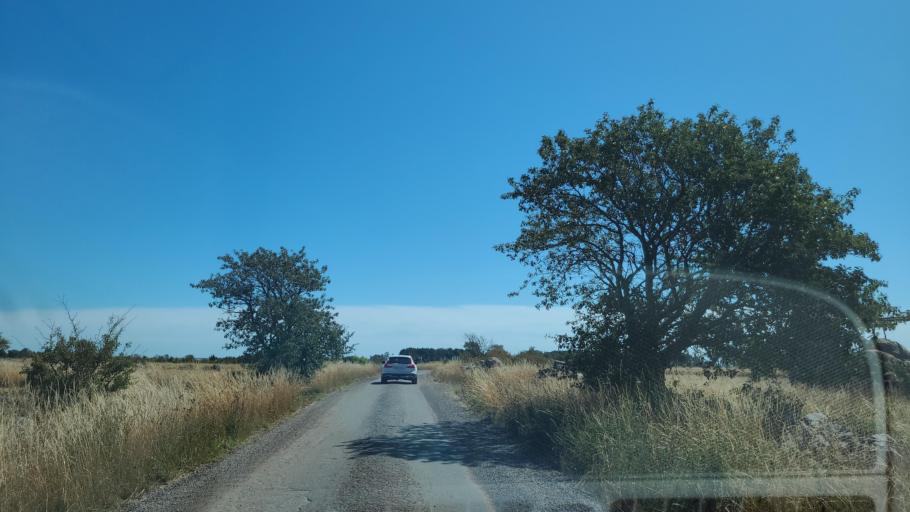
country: SE
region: Kalmar
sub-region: Morbylanga Kommun
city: Sodra Sandby
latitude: 56.7112
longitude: 16.7194
